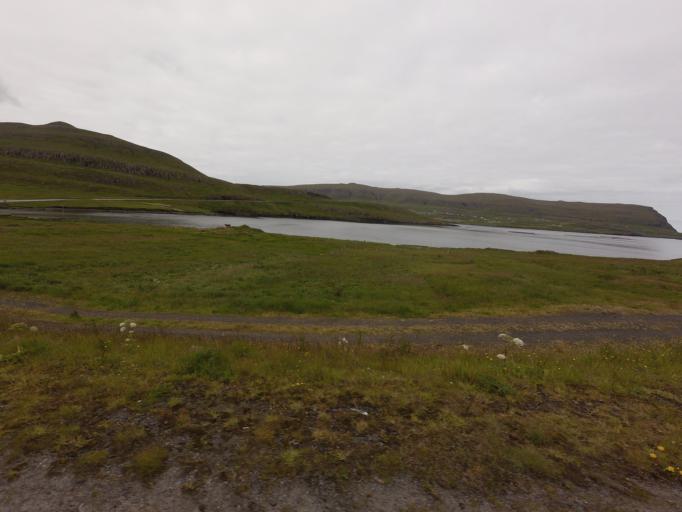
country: FO
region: Suduroy
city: Tvoroyri
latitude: 61.5320
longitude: -6.8069
